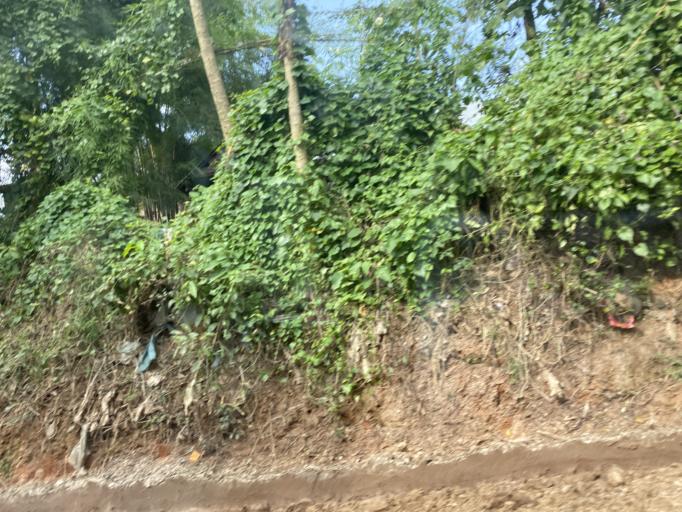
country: IN
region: Tripura
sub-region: West Tripura
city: Agartala
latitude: 23.9872
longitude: 91.2832
